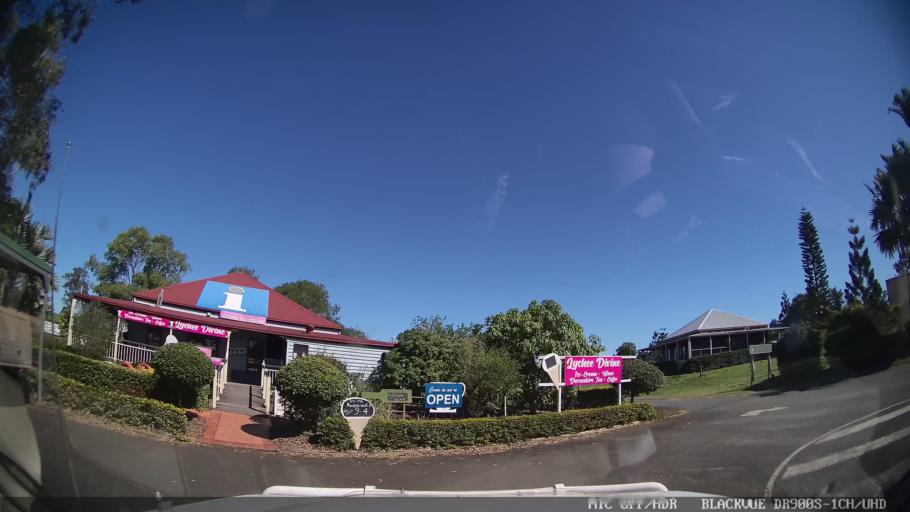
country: AU
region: Queensland
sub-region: Fraser Coast
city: Maryborough
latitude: -25.5773
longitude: 152.6543
